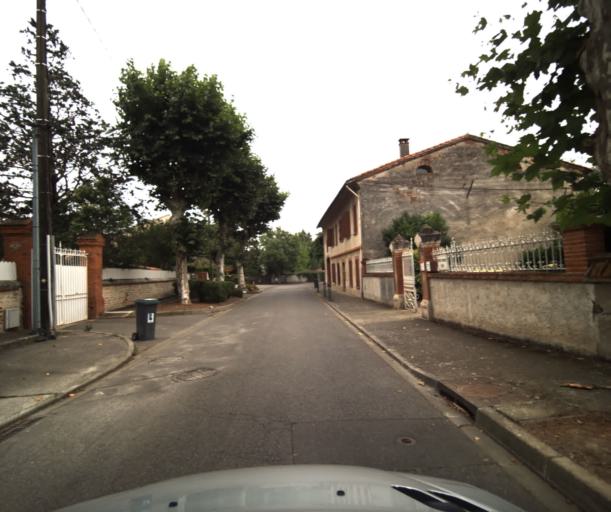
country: FR
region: Midi-Pyrenees
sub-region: Departement de la Haute-Garonne
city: Portet-sur-Garonne
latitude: 43.5245
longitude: 1.4114
